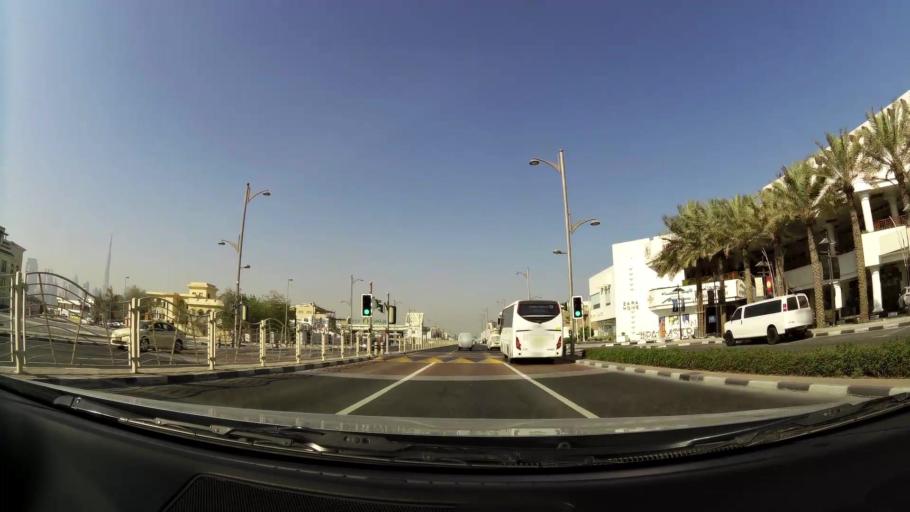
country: AE
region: Ash Shariqah
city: Sharjah
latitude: 25.2337
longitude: 55.2647
